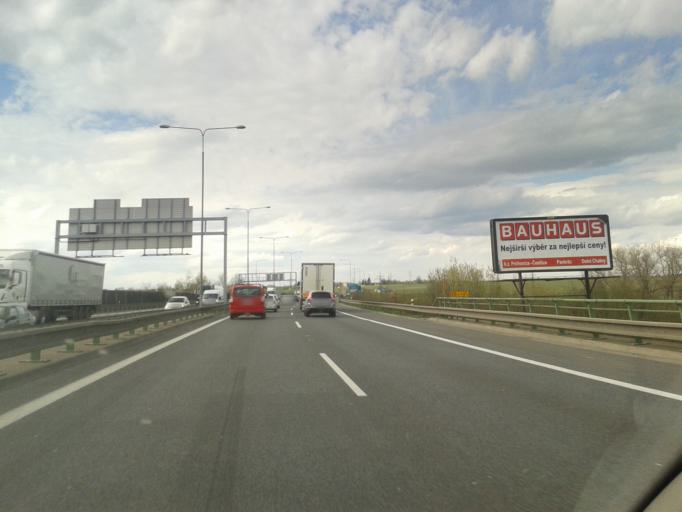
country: CZ
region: Central Bohemia
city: Trebotov
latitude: 50.0271
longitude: 14.2901
